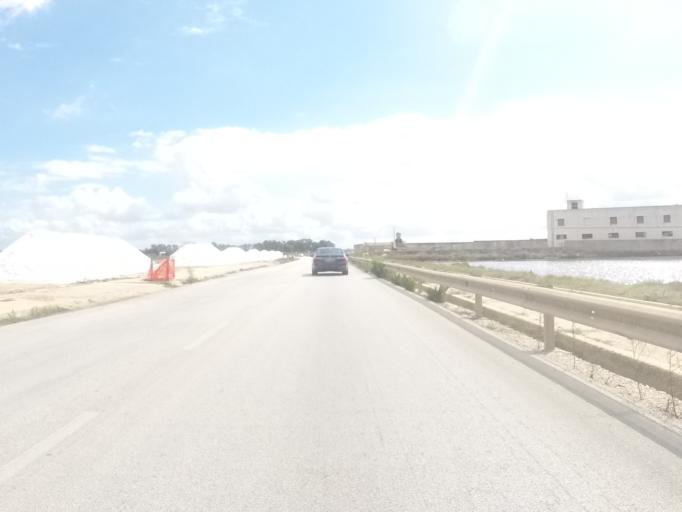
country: IT
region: Sicily
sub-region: Trapani
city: Trapani
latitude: 37.9951
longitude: 12.5348
